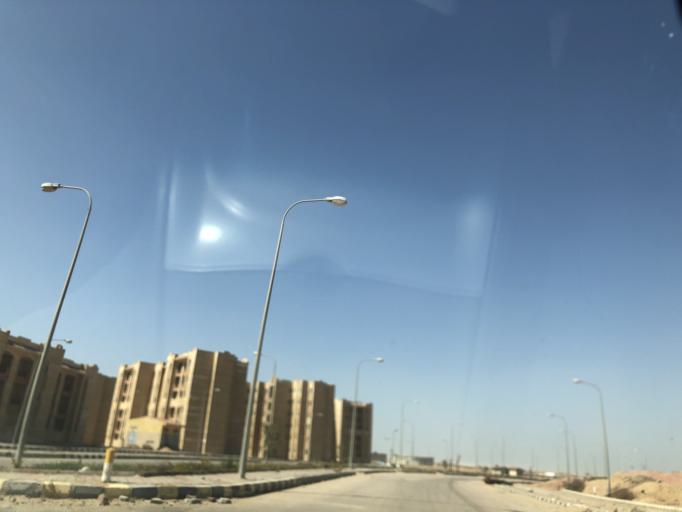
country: EG
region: Al Jizah
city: Madinat Sittah Uktubar
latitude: 29.9238
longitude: 31.0379
